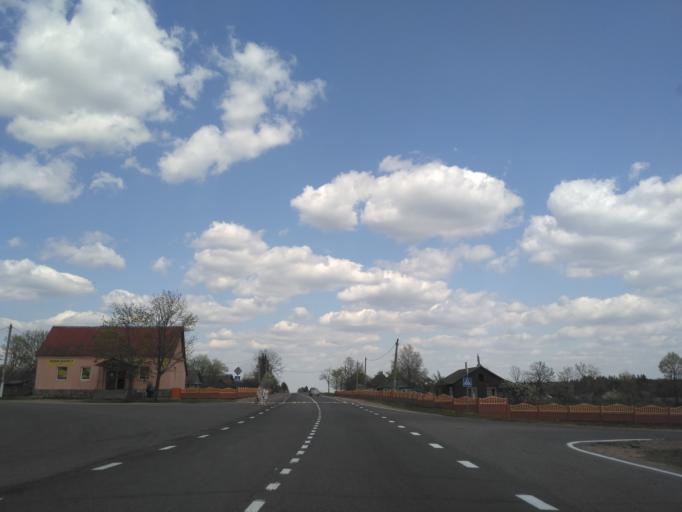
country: BY
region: Minsk
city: Vilyeyka
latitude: 54.5969
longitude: 26.8810
